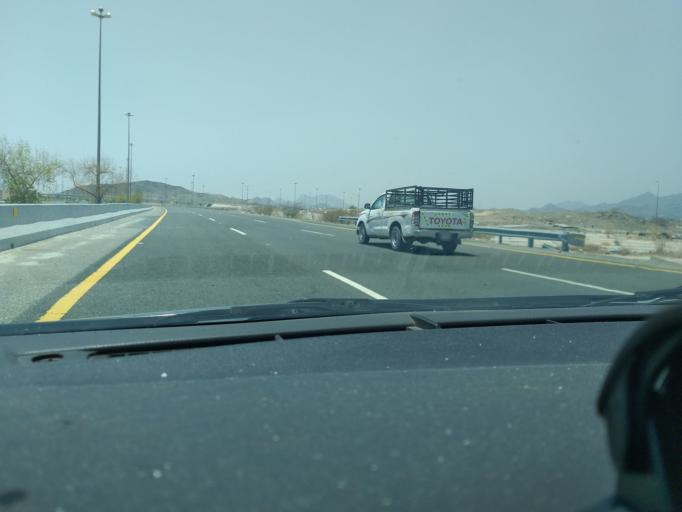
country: SA
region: Makkah
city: Mecca
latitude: 21.3291
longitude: 39.9970
